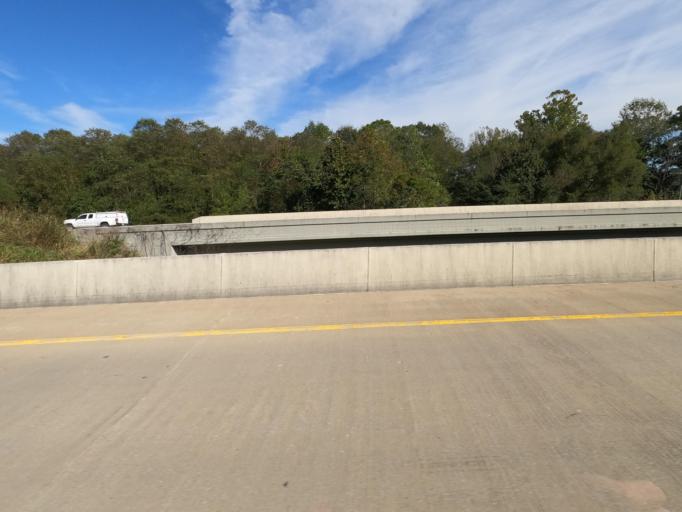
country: US
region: Tennessee
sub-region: Fayette County
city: Piperton
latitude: 35.1169
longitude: -89.6369
